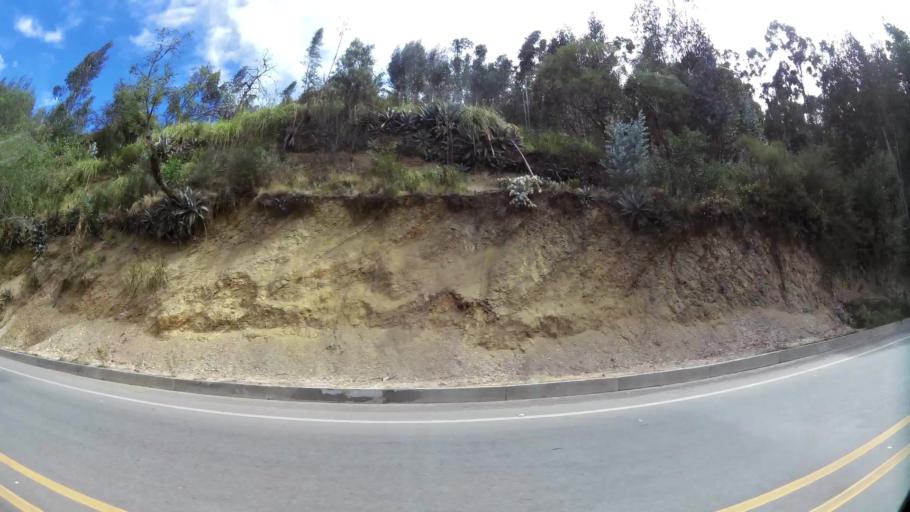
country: EC
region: Canar
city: Azogues
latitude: -2.7256
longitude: -78.8692
